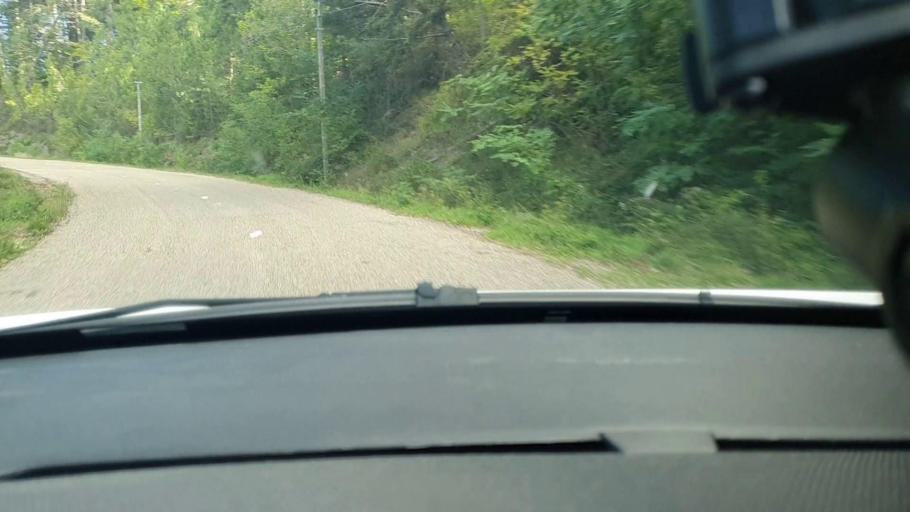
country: FR
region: Rhone-Alpes
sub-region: Departement de l'Ardeche
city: Les Vans
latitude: 44.3963
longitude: 3.9934
